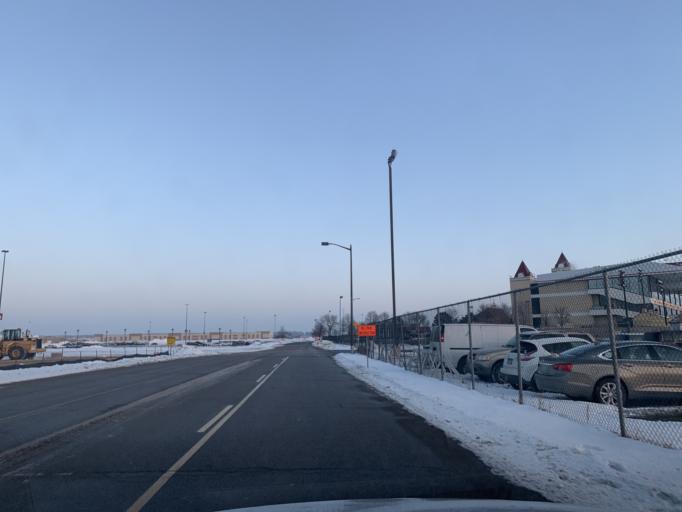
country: US
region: Minnesota
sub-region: Scott County
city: Shakopee
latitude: 44.7885
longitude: -93.4847
